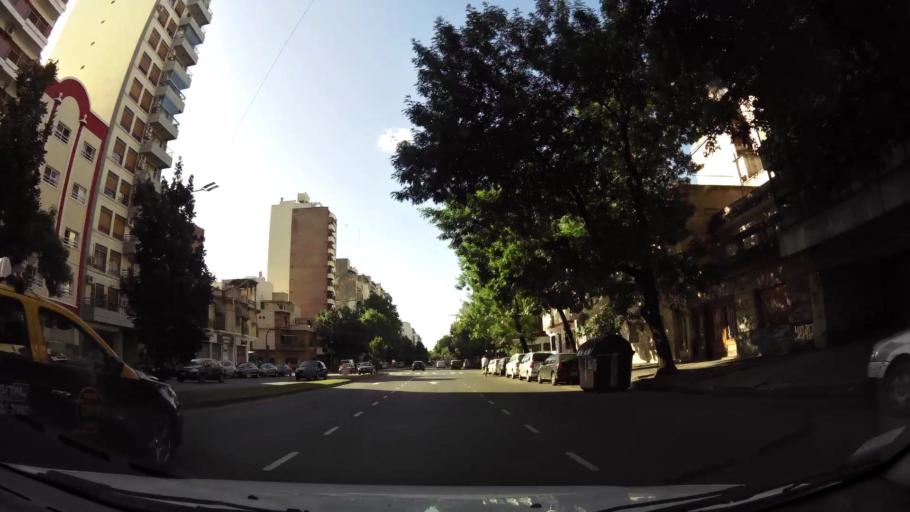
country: AR
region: Buenos Aires F.D.
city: Colegiales
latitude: -34.6094
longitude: -58.4441
